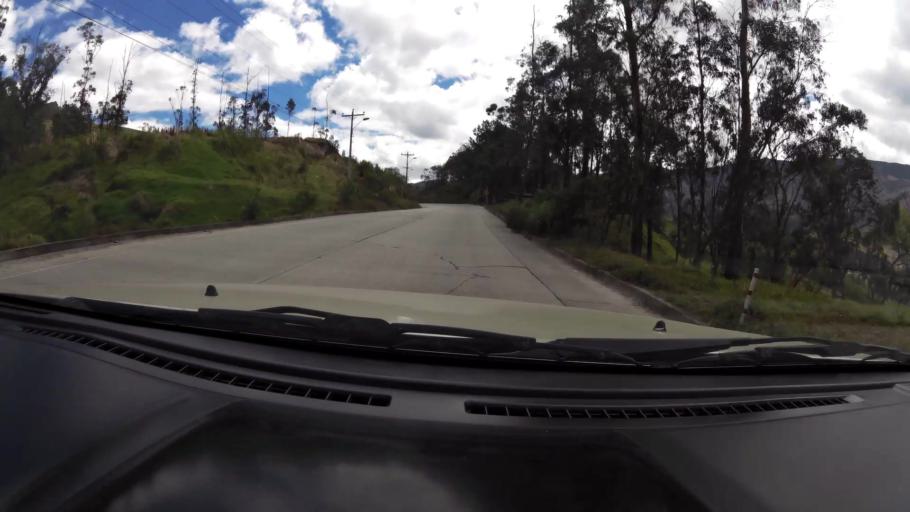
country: EC
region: Azuay
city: Cuenca
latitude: -3.1478
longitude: -79.1454
